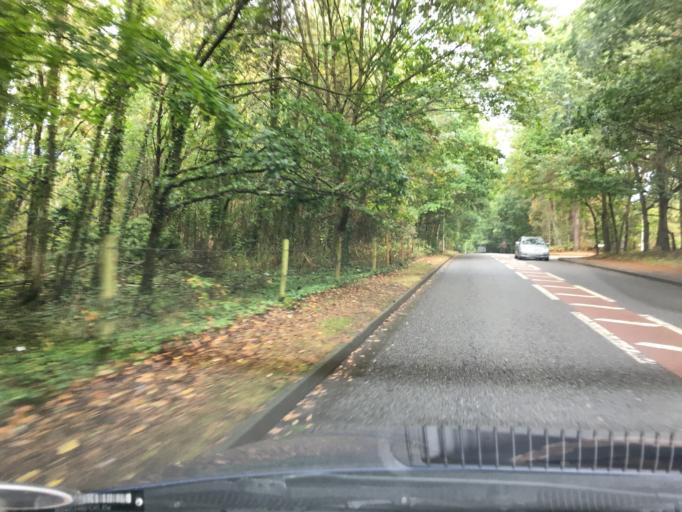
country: GB
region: England
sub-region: Bracknell Forest
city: Crowthorne
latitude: 51.3803
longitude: -0.8056
